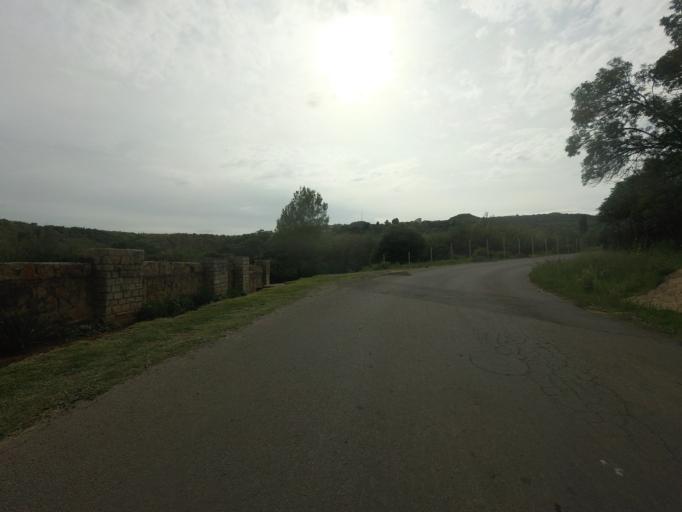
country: LS
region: Maseru
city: Maseru
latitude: -29.3220
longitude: 27.4794
